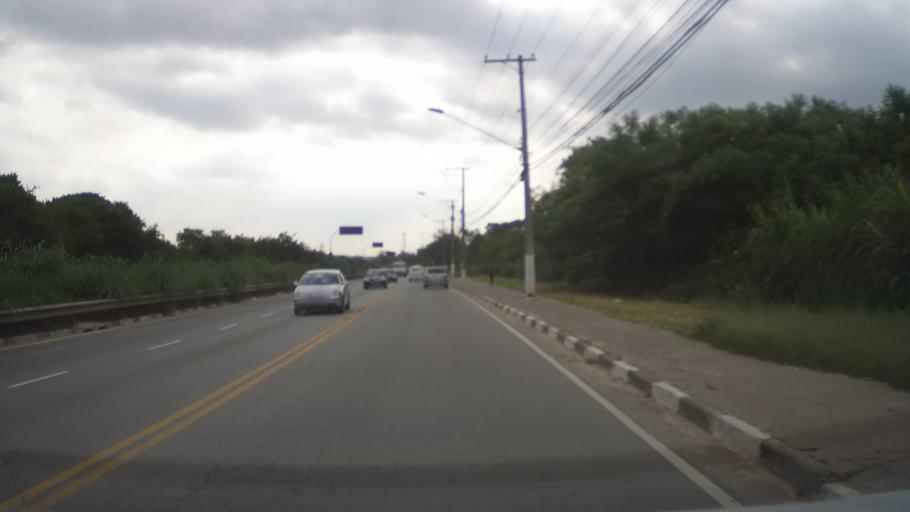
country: BR
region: Sao Paulo
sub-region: Guarulhos
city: Guarulhos
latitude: -23.4173
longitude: -46.4746
